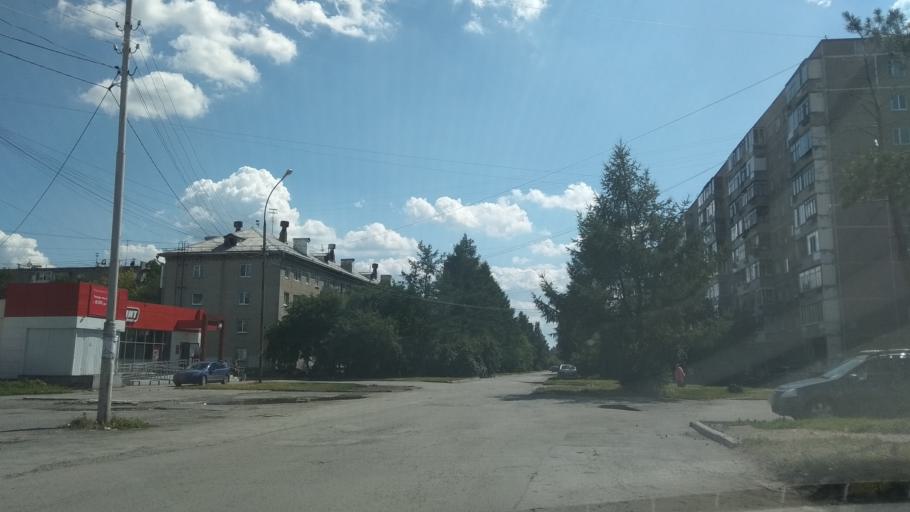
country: RU
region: Sverdlovsk
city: Yekaterinburg
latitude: 56.8344
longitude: 60.6898
